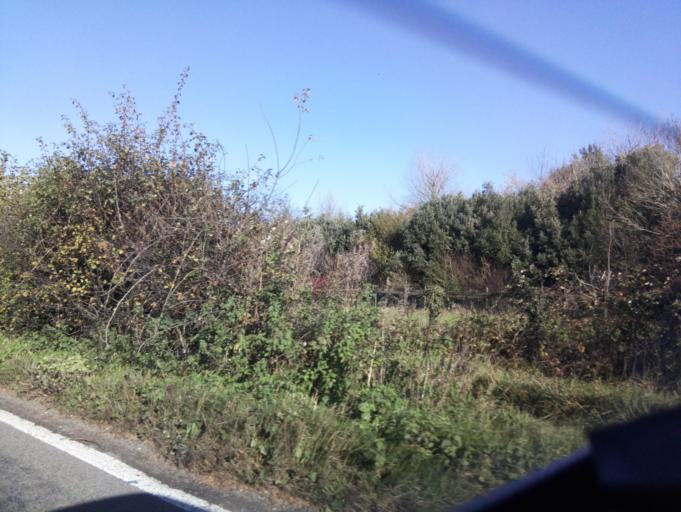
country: GB
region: England
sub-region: Somerset
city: Yeovil
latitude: 50.9021
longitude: -2.6217
